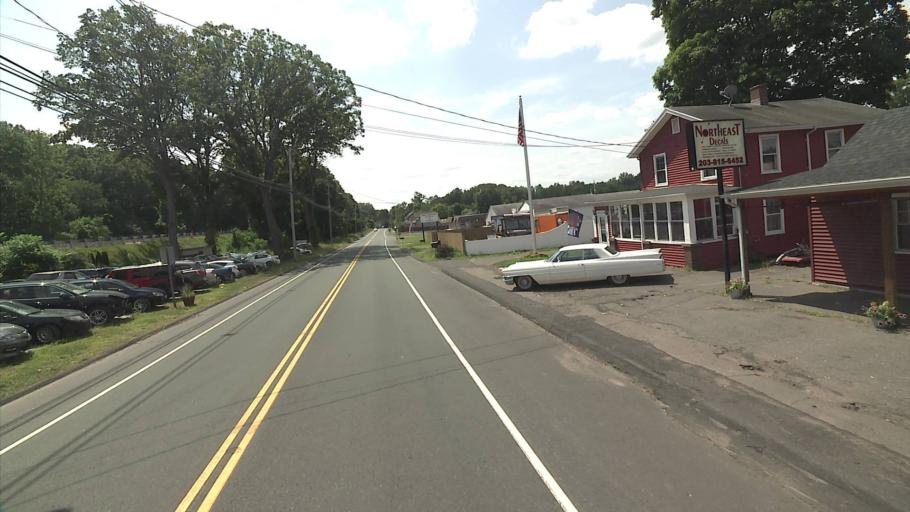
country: US
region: Connecticut
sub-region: New Haven County
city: Meriden
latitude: 41.5051
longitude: -72.8167
